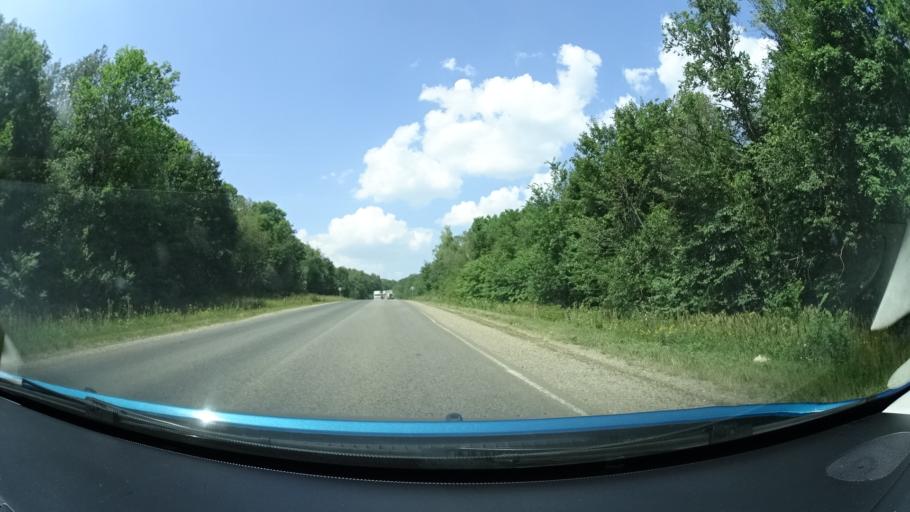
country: RU
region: Bashkortostan
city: Oktyabr'skiy
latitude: 54.4574
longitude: 53.5829
